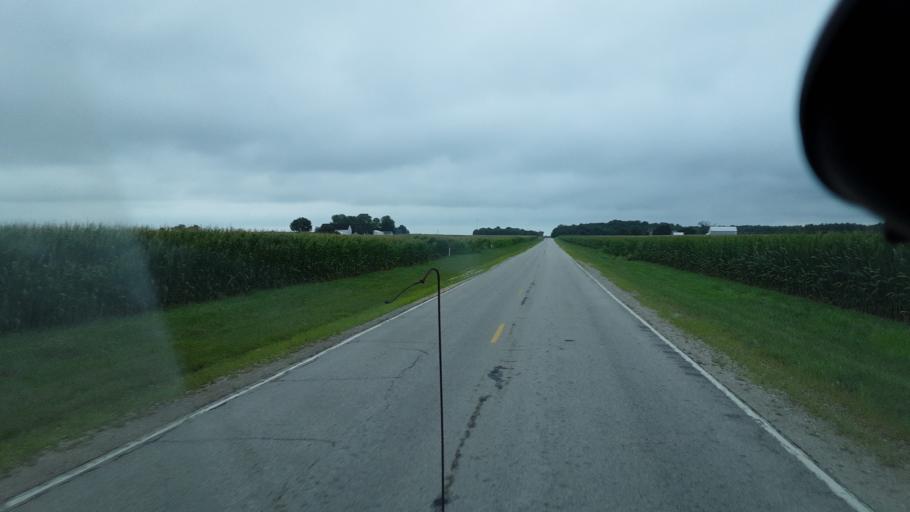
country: US
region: Indiana
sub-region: Wells County
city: Bluffton
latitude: 40.7349
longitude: -85.0894
